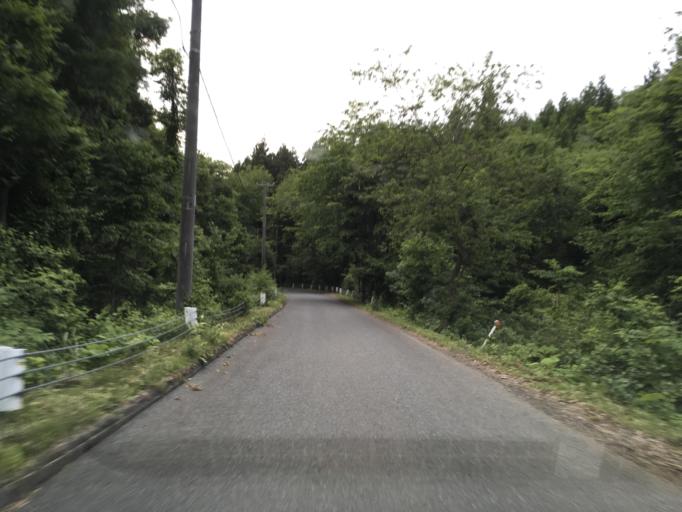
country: JP
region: Iwate
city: Mizusawa
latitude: 39.1522
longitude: 141.2956
